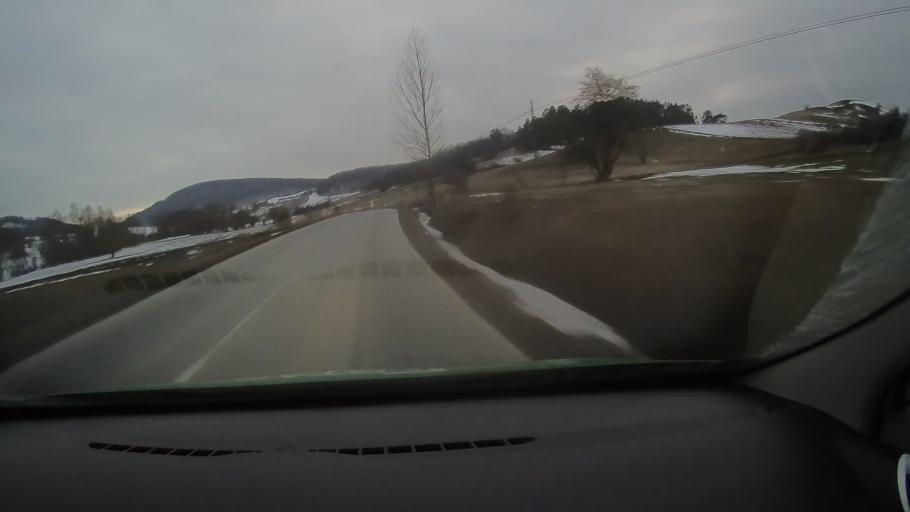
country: RO
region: Harghita
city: Taureni
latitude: 46.2346
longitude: 25.2461
